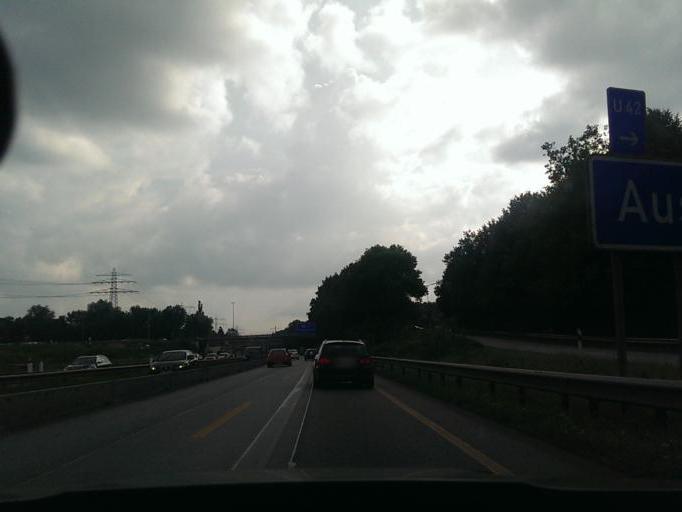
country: DE
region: Schleswig-Holstein
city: Bonningstedt
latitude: 53.6362
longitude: 9.9243
